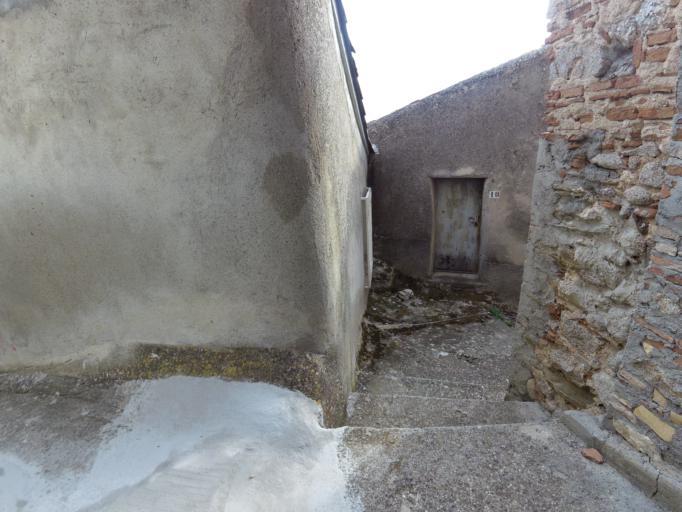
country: IT
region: Calabria
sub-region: Provincia di Reggio Calabria
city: Stignano
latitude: 38.4166
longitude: 16.4717
